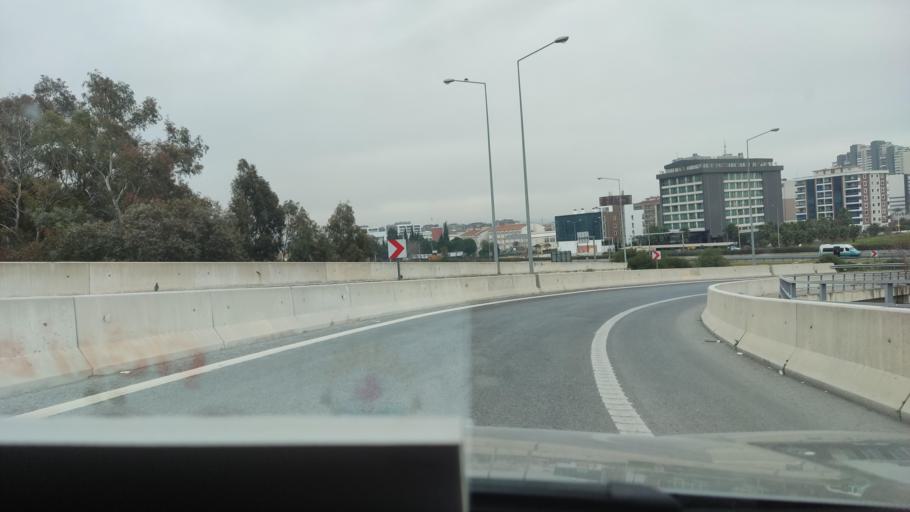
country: TR
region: Izmir
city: Karsiyaka
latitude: 38.4852
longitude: 27.0844
